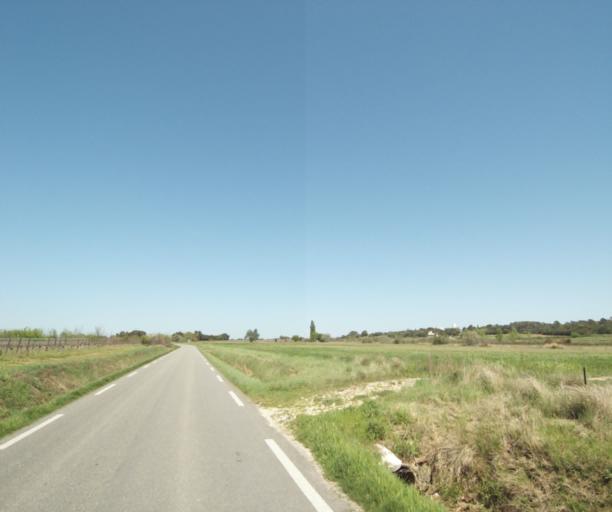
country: FR
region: Languedoc-Roussillon
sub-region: Departement de l'Herault
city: Sussargues
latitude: 43.7252
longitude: 4.0083
